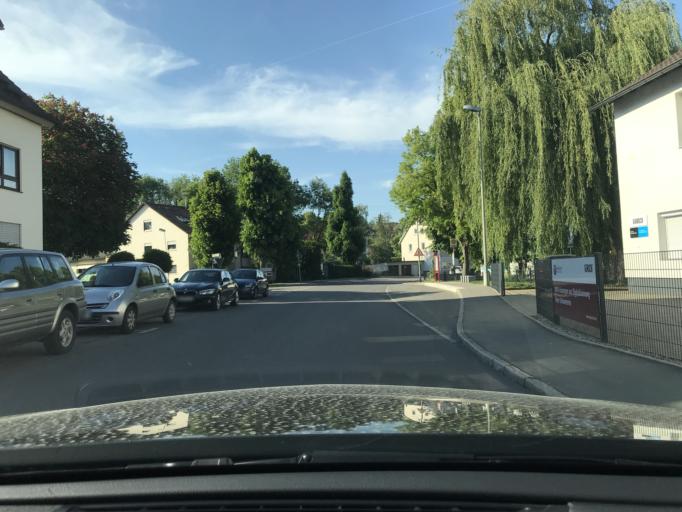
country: DE
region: Baden-Wuerttemberg
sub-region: Regierungsbezirk Stuttgart
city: Affalterbach
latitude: 48.8889
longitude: 9.3127
